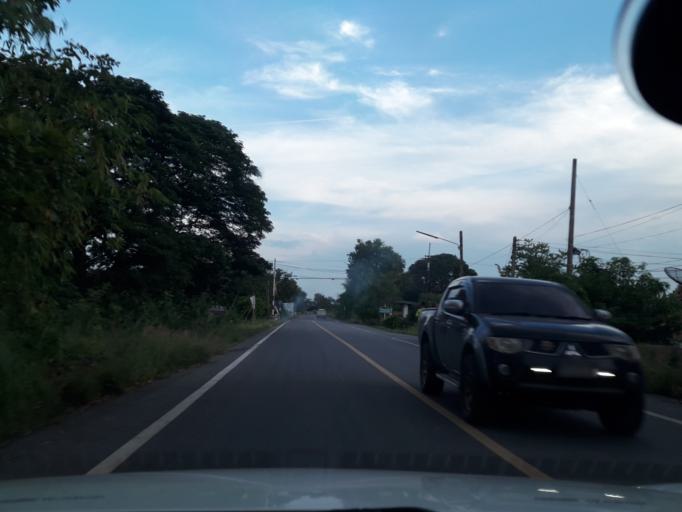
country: TH
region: Sara Buri
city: Nong Khae
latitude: 14.3072
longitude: 100.8871
